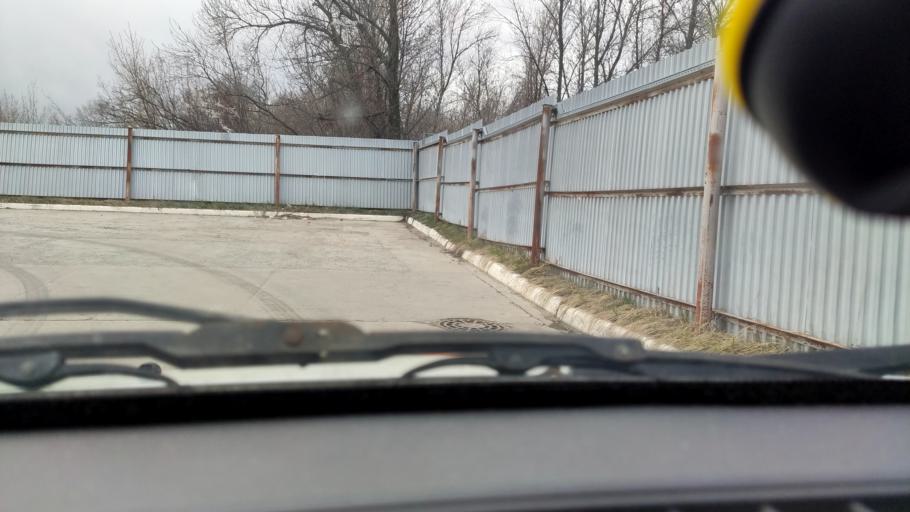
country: RU
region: Samara
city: Tol'yatti
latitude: 53.5242
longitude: 49.2557
